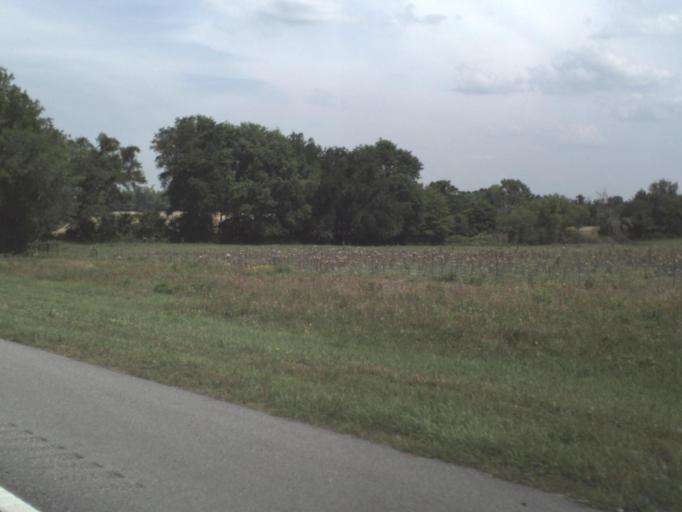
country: US
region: Florida
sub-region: Suwannee County
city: Live Oak
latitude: 30.3522
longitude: -83.0361
